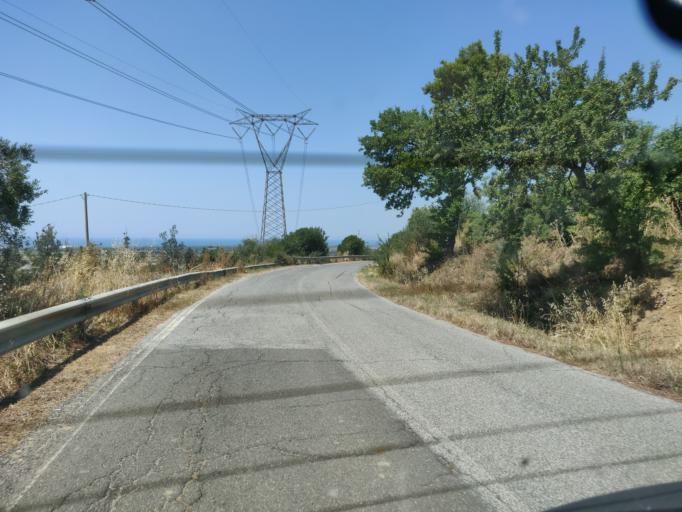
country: IT
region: Latium
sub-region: Citta metropolitana di Roma Capitale
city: Aurelia
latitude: 42.1344
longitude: 11.8238
